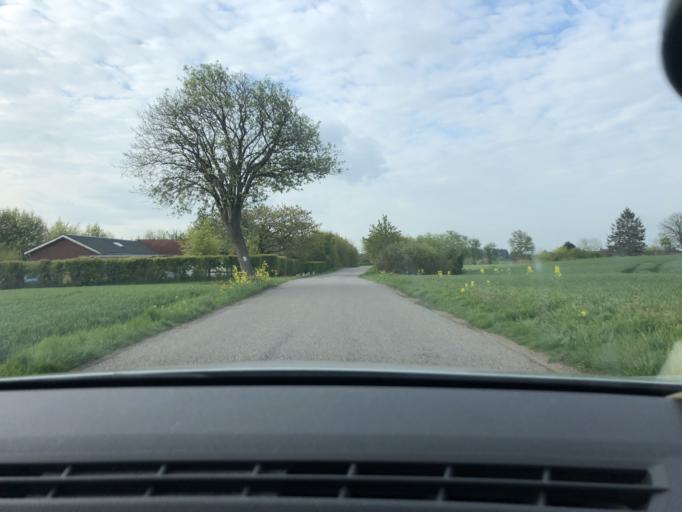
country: DK
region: Zealand
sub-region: Faxe Kommune
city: Ronnede
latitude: 55.2331
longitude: 12.0516
